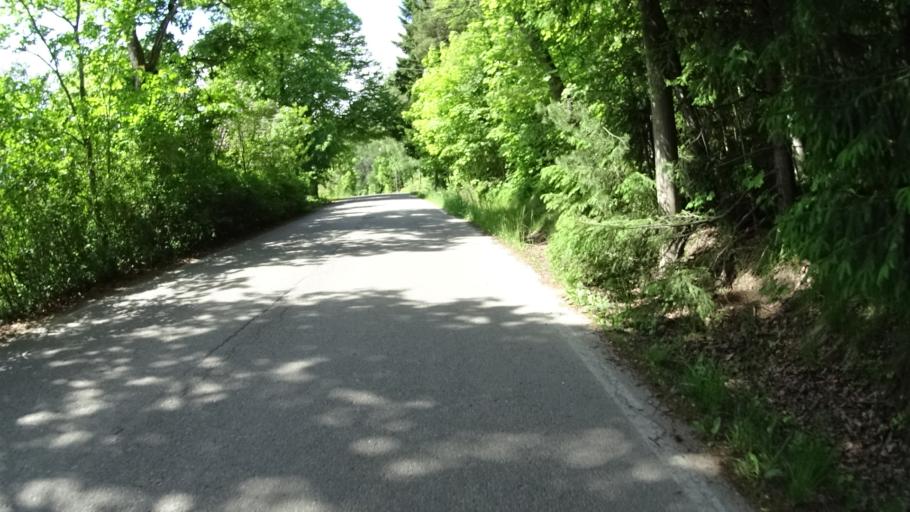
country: FI
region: Uusimaa
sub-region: Helsinki
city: Kauniainen
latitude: 60.2941
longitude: 24.6830
